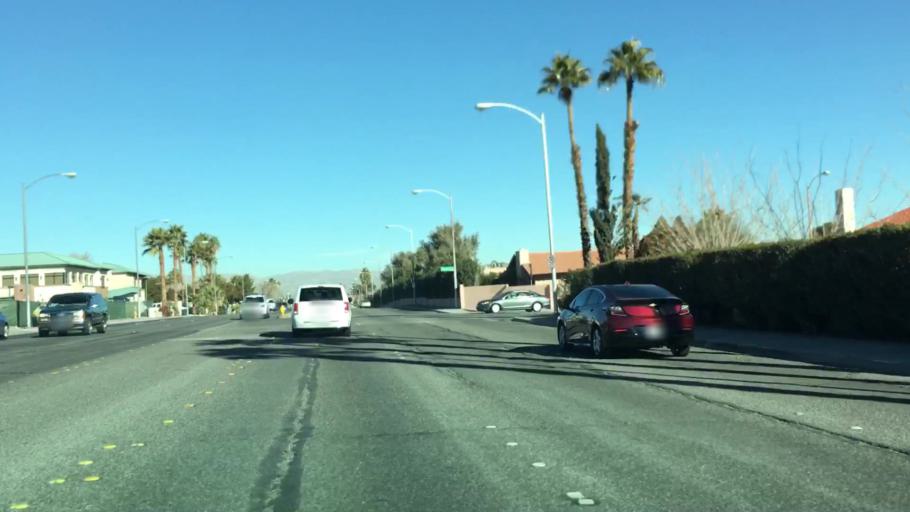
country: US
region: Nevada
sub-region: Clark County
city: Winchester
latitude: 36.1256
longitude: -115.1187
